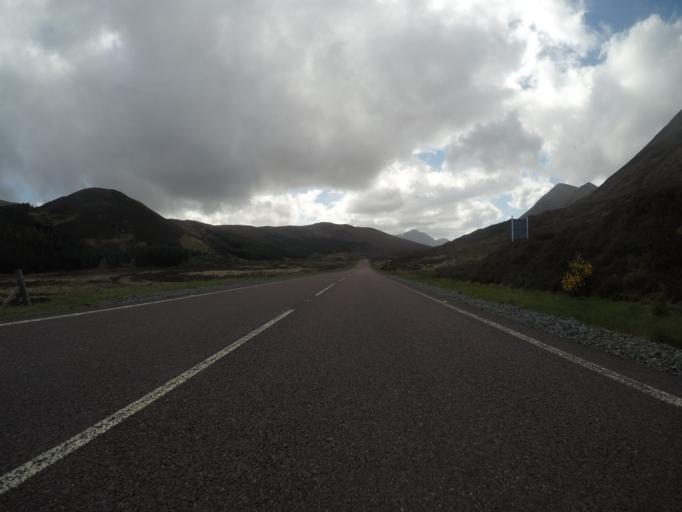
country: GB
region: Scotland
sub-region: Highland
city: Portree
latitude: 57.3048
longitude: -6.0909
